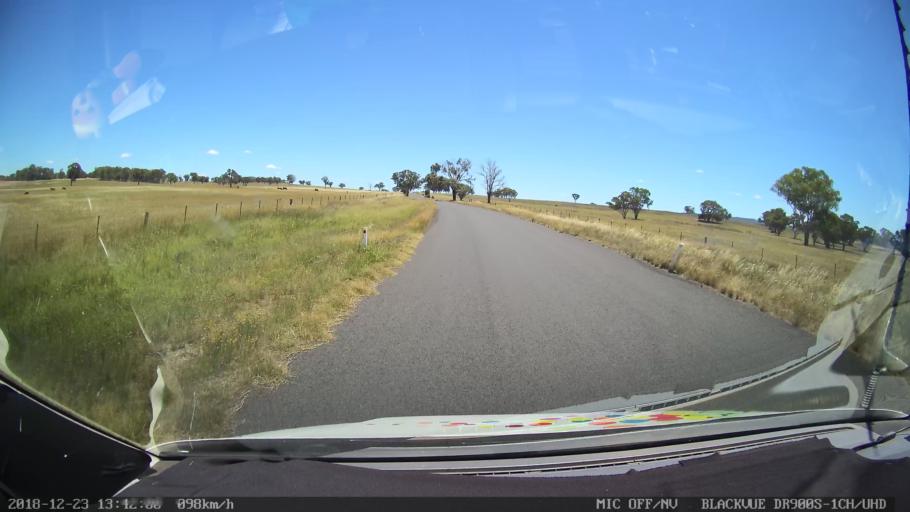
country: AU
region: New South Wales
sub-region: Armidale Dumaresq
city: Armidale
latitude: -30.4720
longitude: 151.1676
